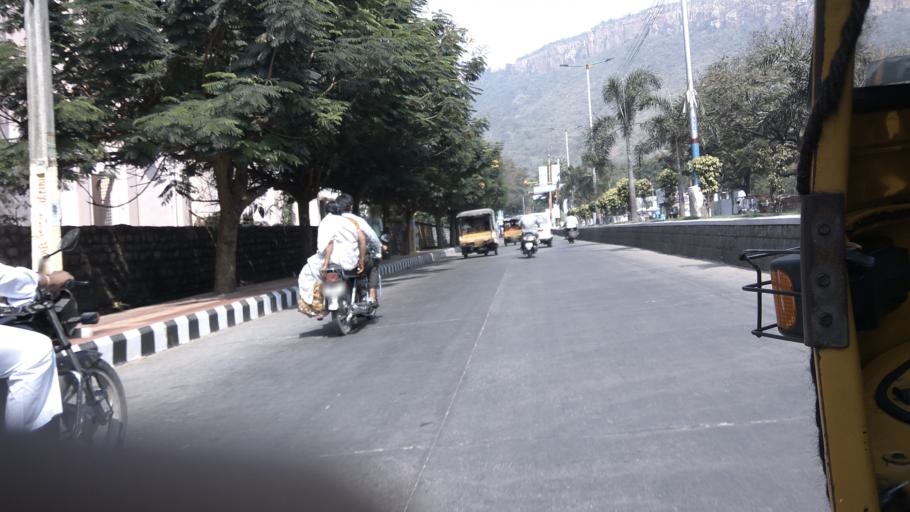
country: IN
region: Andhra Pradesh
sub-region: Chittoor
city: Akkarampalle
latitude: 13.6440
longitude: 79.4079
